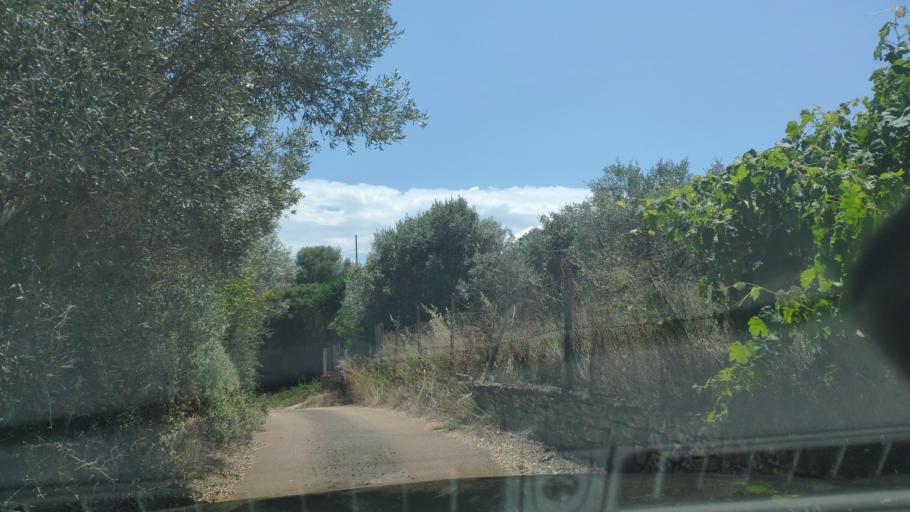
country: GR
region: West Greece
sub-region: Nomos Aitolias kai Akarnanias
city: Amfilochia
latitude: 38.9091
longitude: 21.1063
